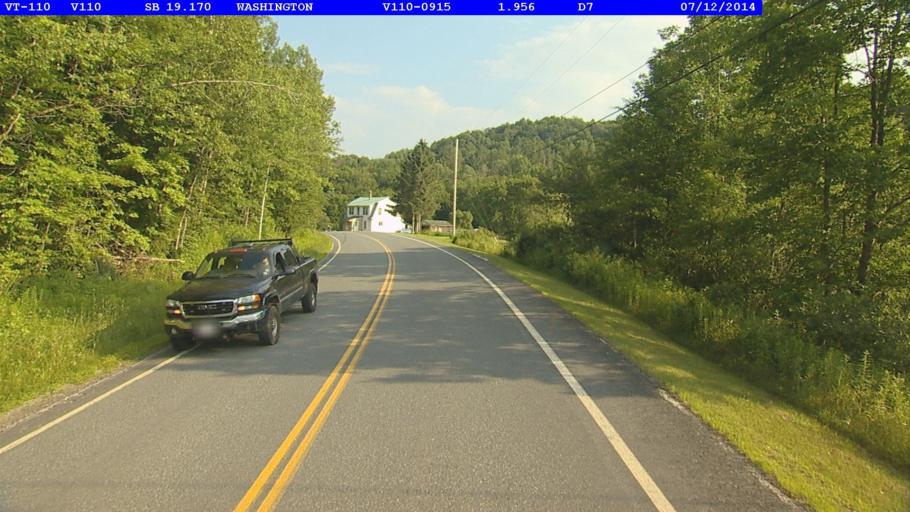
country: US
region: Vermont
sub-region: Orange County
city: Chelsea
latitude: 44.0640
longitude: -72.4673
